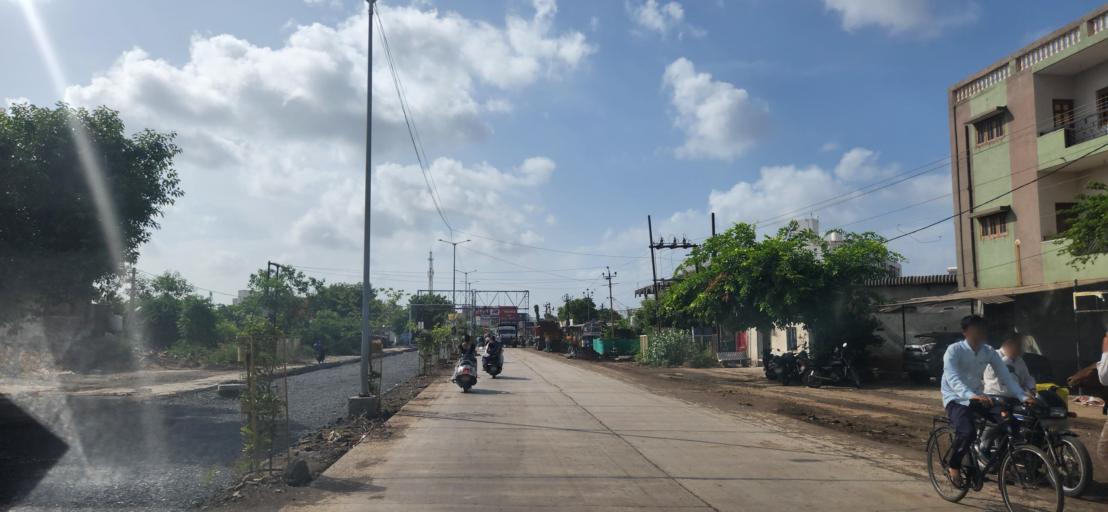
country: IN
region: Gujarat
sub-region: Bhavnagar
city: Bhavnagar
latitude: 21.7351
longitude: 72.1511
